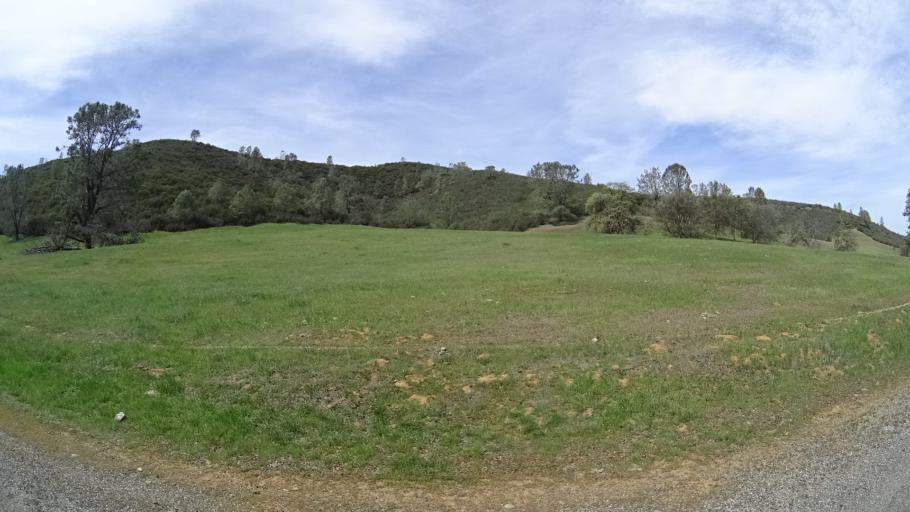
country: US
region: California
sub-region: Glenn County
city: Willows
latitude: 39.6002
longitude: -122.5276
